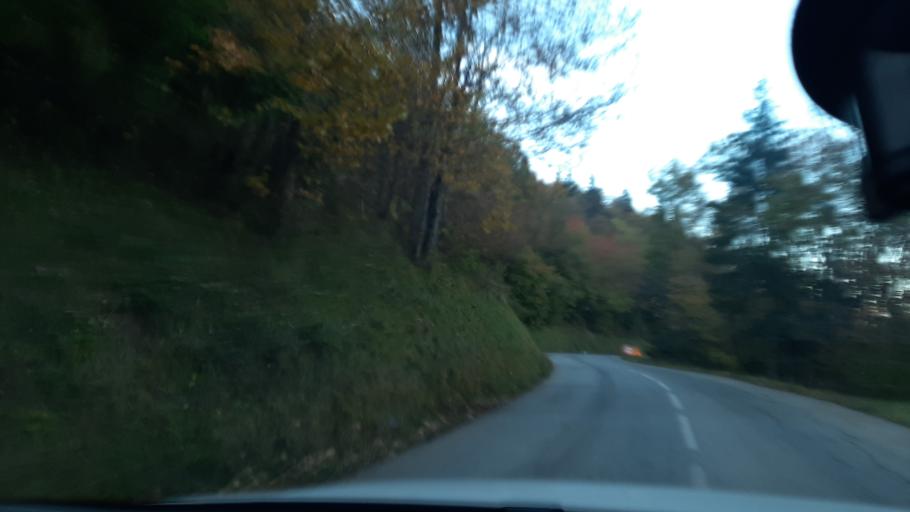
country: FR
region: Rhone-Alpes
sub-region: Departement de la Savoie
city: Saint-Jean-de-Maurienne
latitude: 45.2030
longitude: 6.3066
